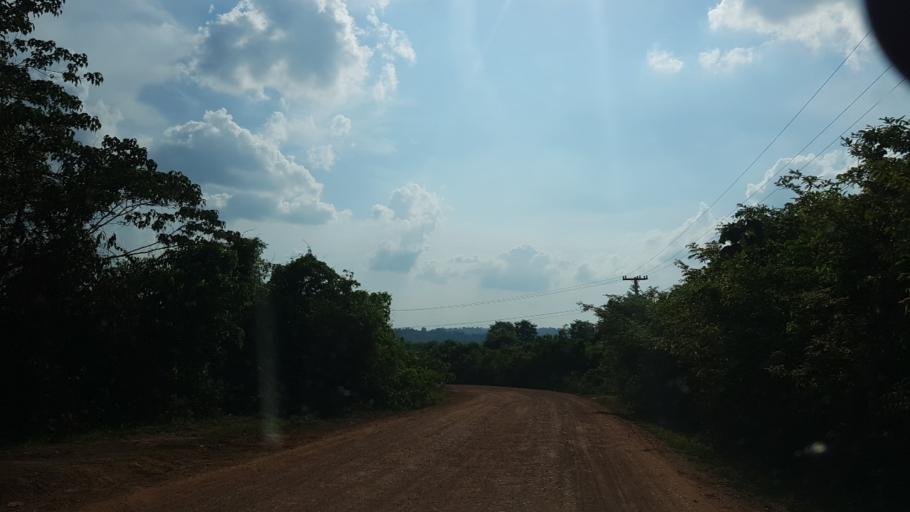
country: LA
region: Vientiane
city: Muang Phon-Hong
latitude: 18.3457
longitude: 102.3015
